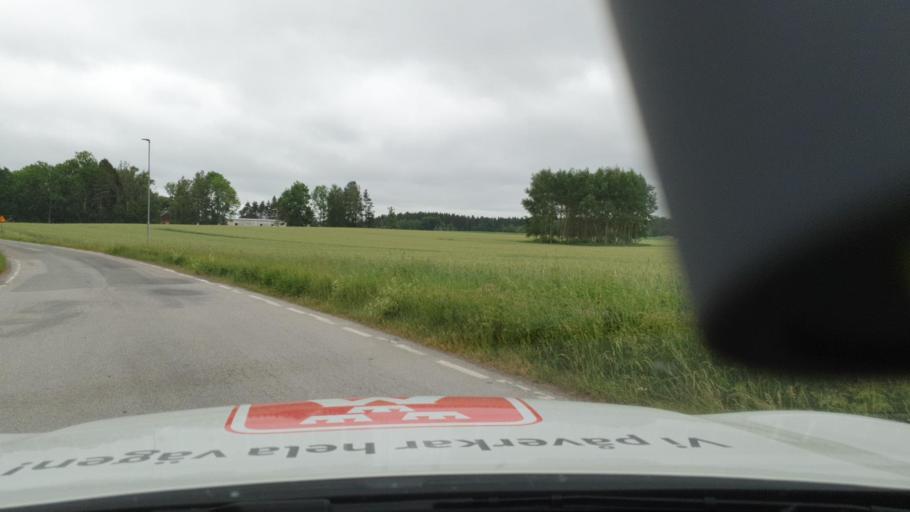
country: SE
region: Vaestra Goetaland
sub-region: Tibro Kommun
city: Tibro
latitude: 58.4054
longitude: 14.1323
